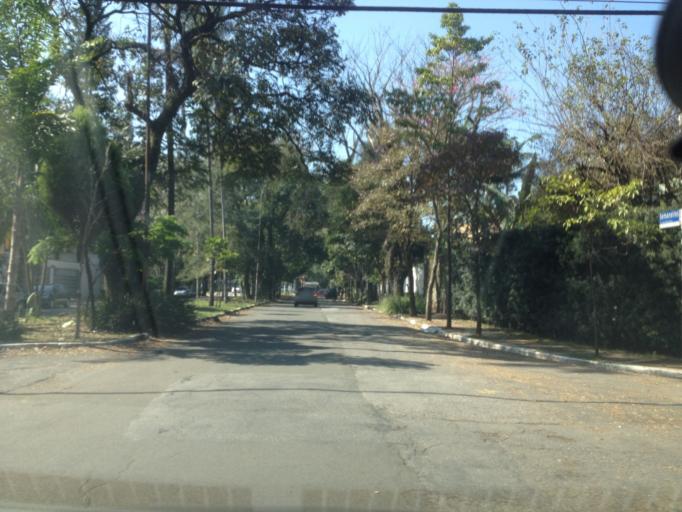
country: BR
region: Sao Paulo
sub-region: Sao Paulo
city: Sao Paulo
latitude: -23.5563
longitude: -46.7065
